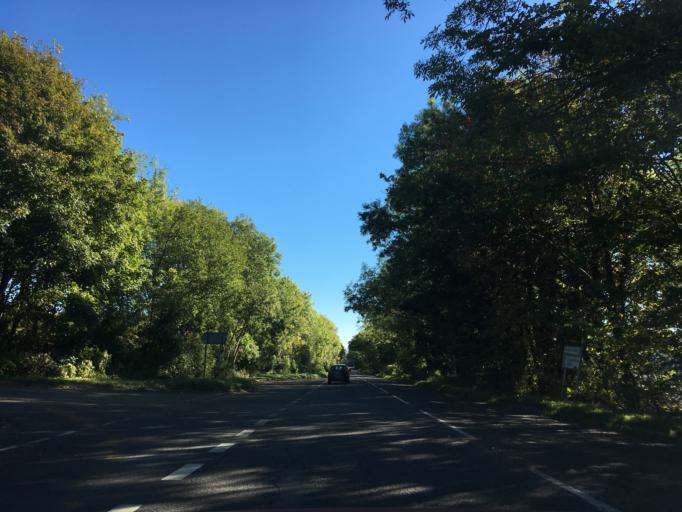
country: GB
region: England
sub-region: Wiltshire
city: Nettleton
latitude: 51.4707
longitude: -2.2578
